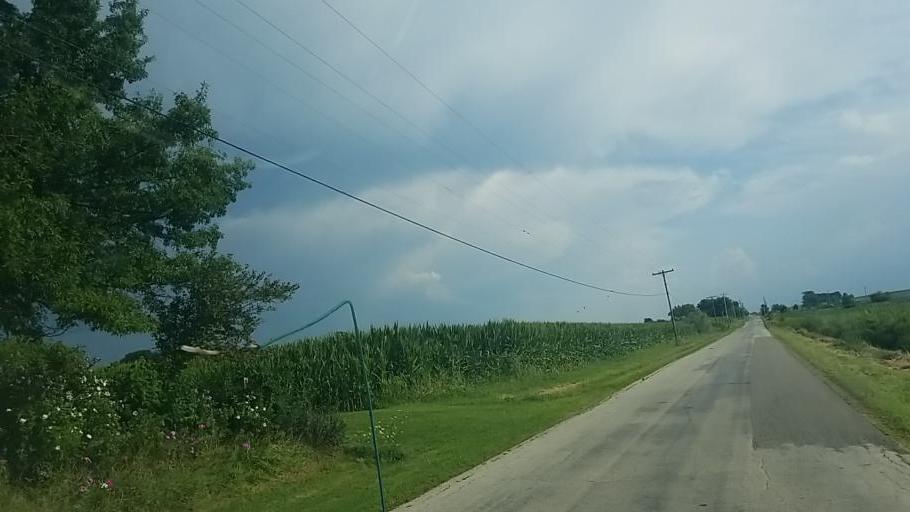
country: US
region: Ohio
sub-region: Wayne County
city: Smithville
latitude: 40.8931
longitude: -81.8611
